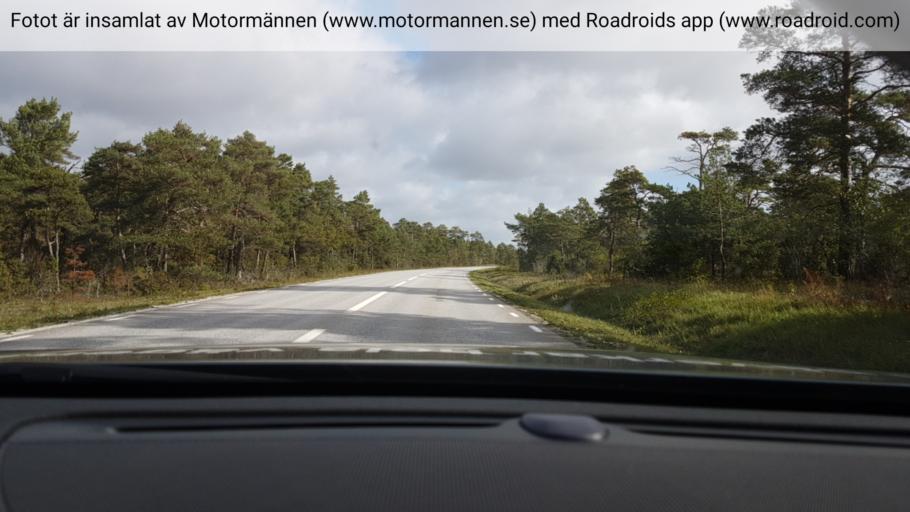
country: SE
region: Gotland
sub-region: Gotland
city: Slite
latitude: 57.8364
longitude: 18.9293
